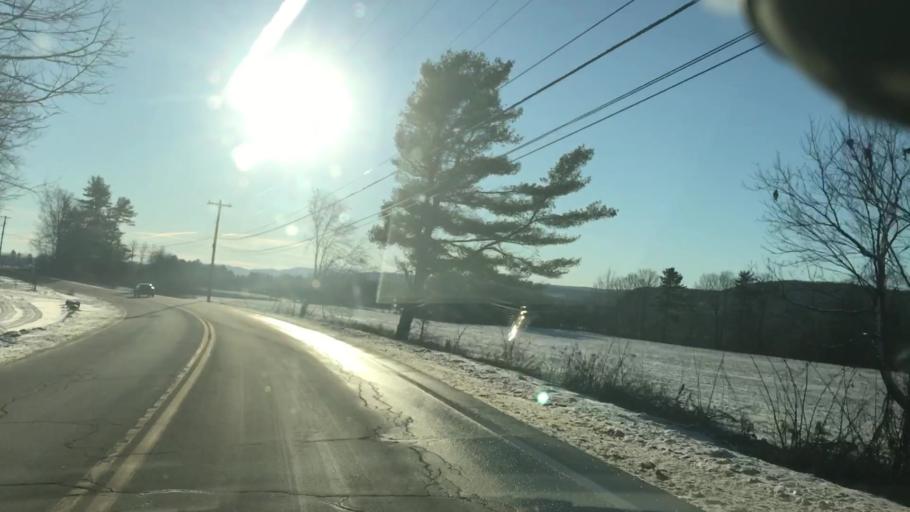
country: US
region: New Hampshire
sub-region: Grafton County
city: North Haverhill
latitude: 44.0664
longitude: -72.0474
